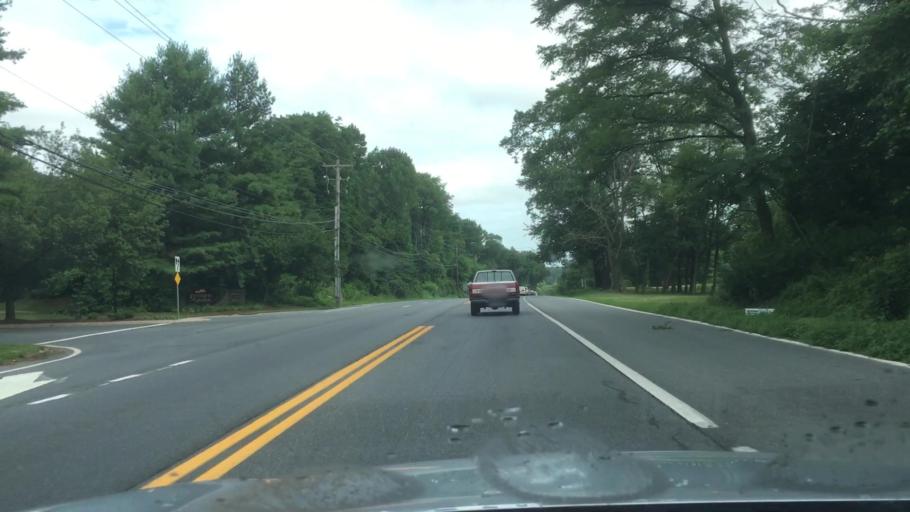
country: US
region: Delaware
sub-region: New Castle County
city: North Star
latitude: 39.7822
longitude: -75.7220
